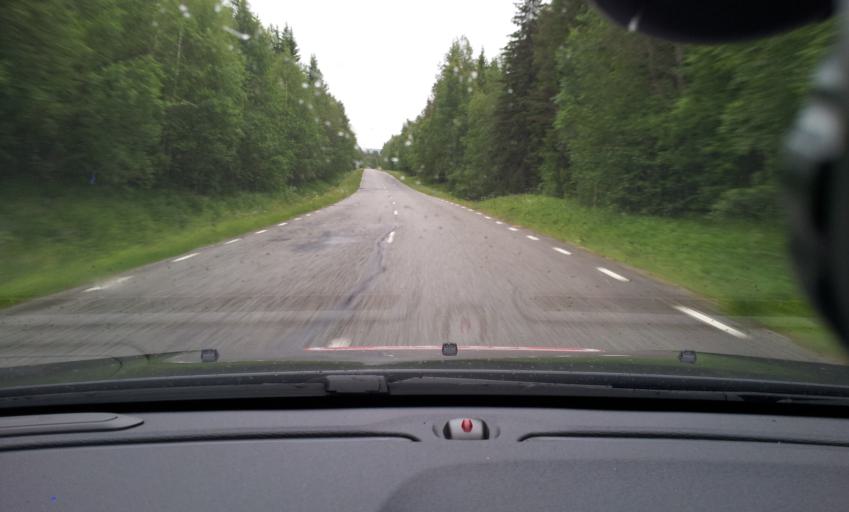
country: SE
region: Jaemtland
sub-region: Ragunda Kommun
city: Hammarstrand
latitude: 63.2376
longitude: 15.9175
